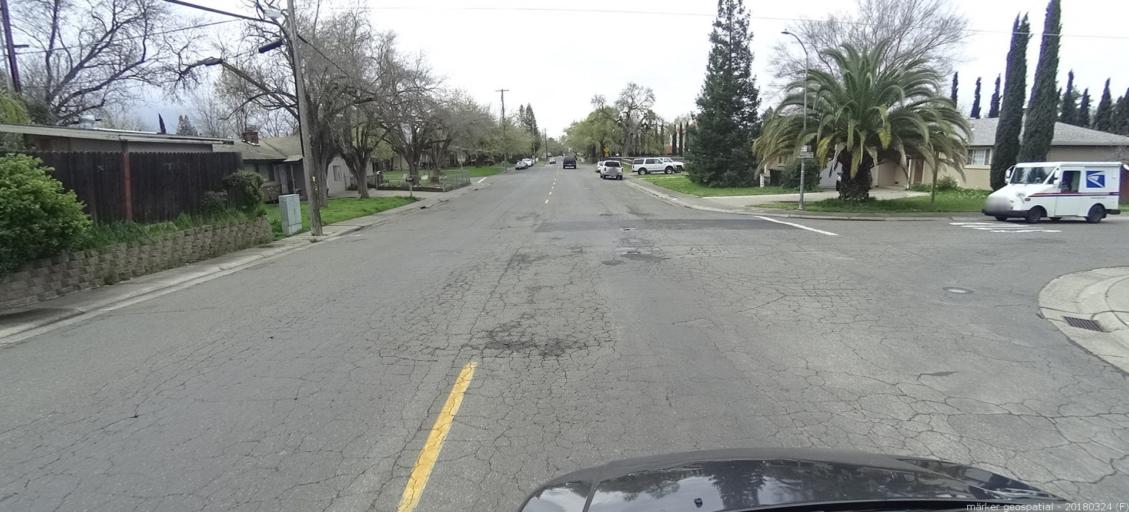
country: US
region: California
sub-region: Sacramento County
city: North Highlands
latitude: 38.6568
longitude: -121.3737
